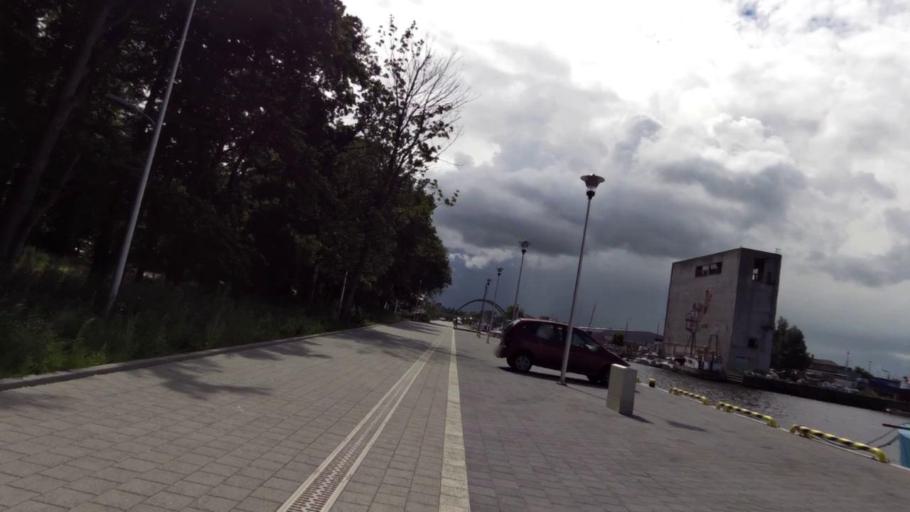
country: PL
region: West Pomeranian Voivodeship
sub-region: Powiat slawienski
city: Darlowo
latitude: 54.4269
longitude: 16.3969
